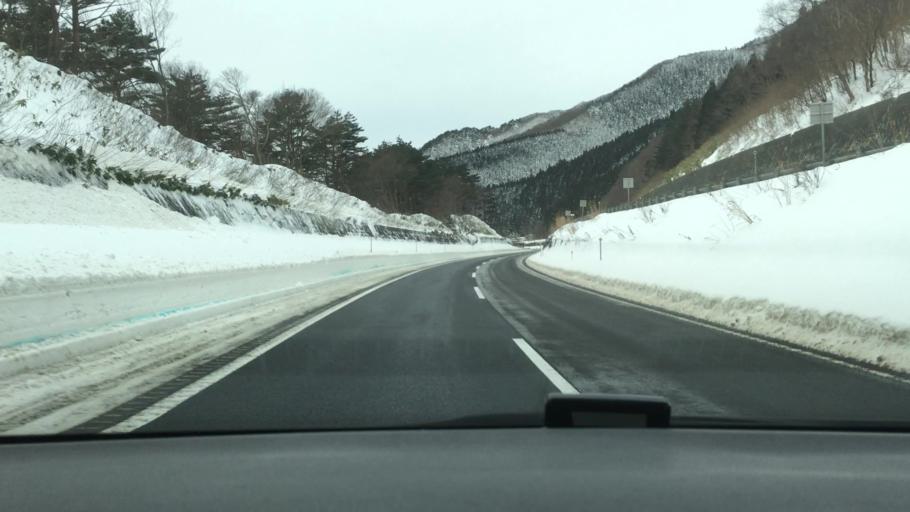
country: JP
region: Akita
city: Hanawa
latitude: 40.1217
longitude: 140.8432
